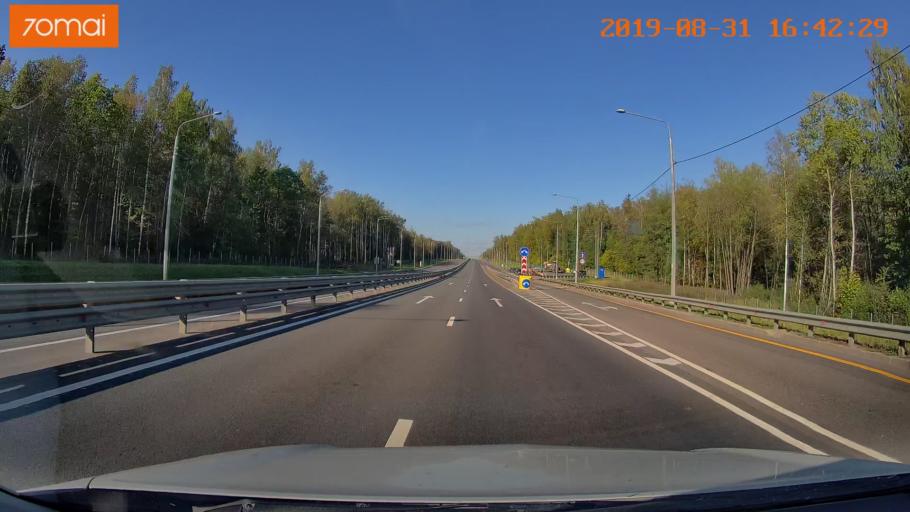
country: RU
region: Kaluga
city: Mstikhino
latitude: 54.5949
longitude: 36.0862
